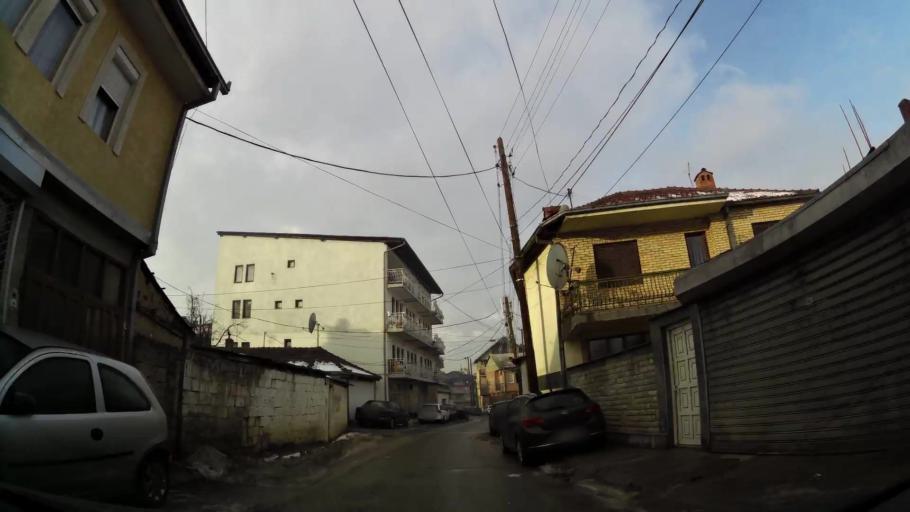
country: XK
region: Pristina
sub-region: Komuna e Prishtines
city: Pristina
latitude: 42.6654
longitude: 21.1722
